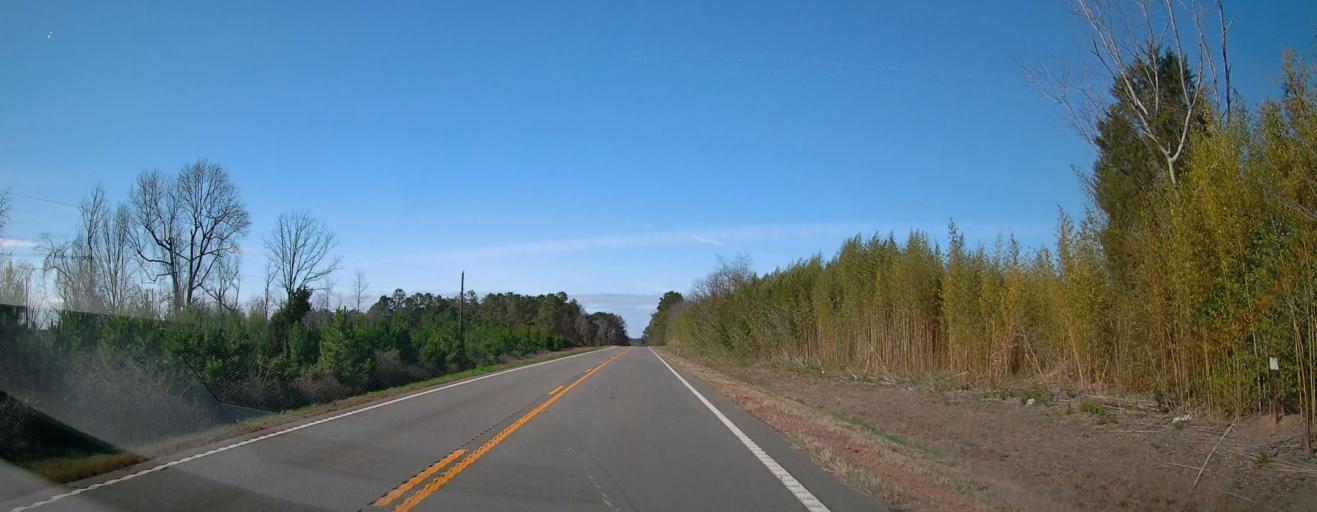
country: US
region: Georgia
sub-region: Macon County
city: Oglethorpe
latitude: 32.3559
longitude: -84.1757
